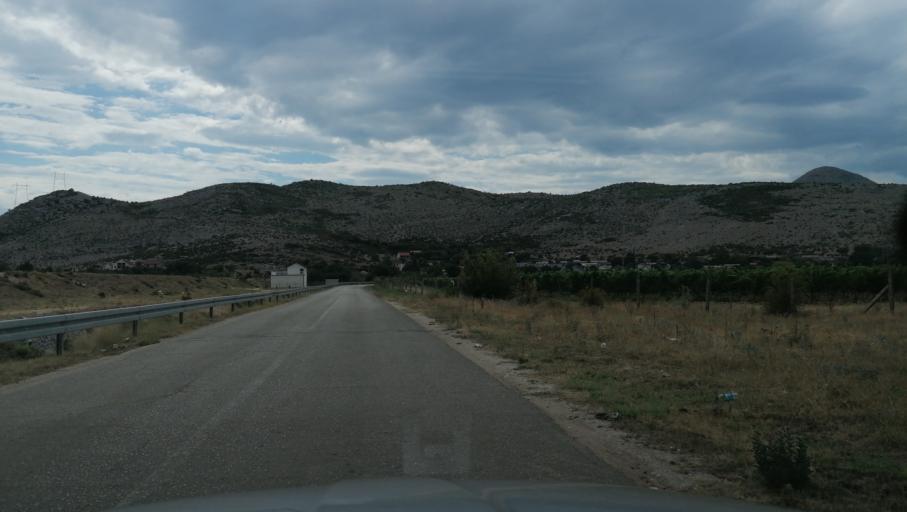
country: BA
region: Republika Srpska
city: Trebinje
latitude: 42.6688
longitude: 18.3276
